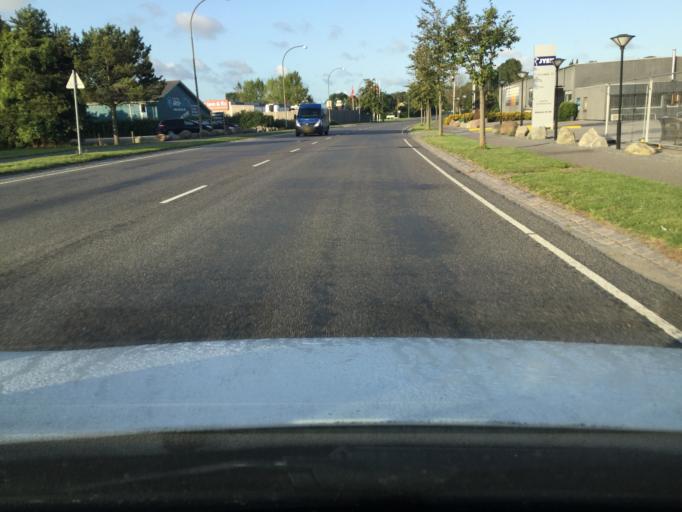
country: DK
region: Zealand
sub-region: Lolland Kommune
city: Nakskov
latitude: 54.8250
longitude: 11.1593
